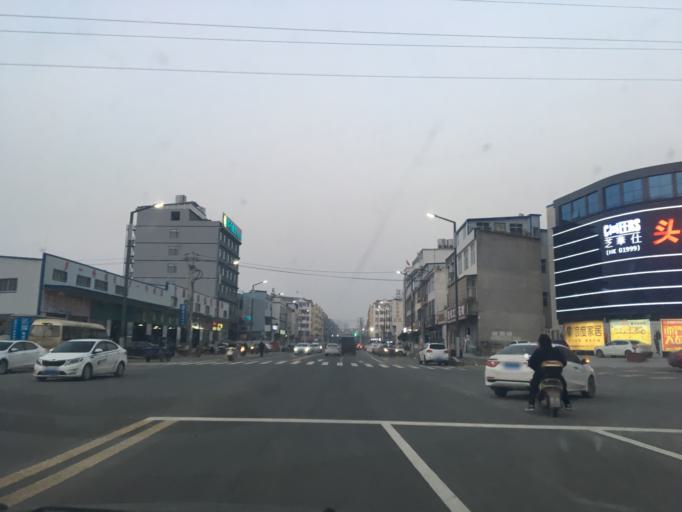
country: CN
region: Hubei
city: Gulou
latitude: 31.1678
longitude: 115.0298
